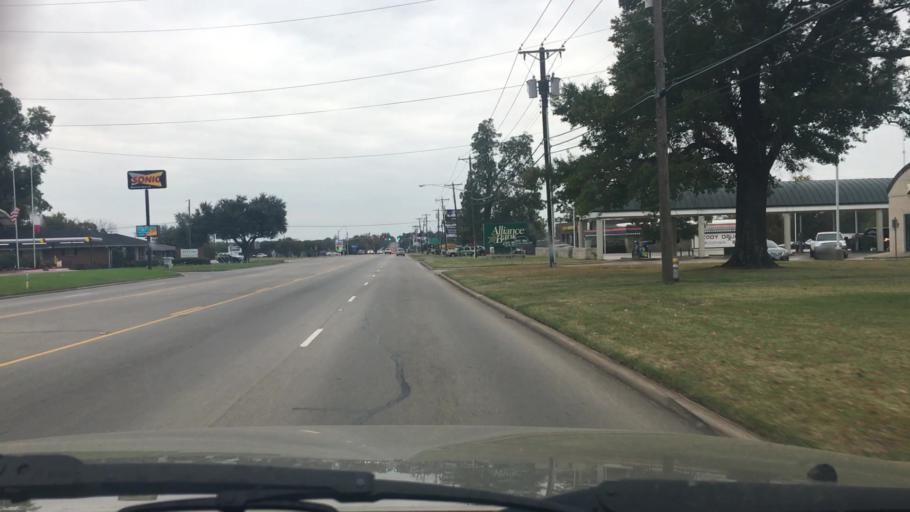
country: US
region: Texas
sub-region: Hopkins County
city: Sulphur Springs
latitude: 33.1119
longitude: -95.5968
